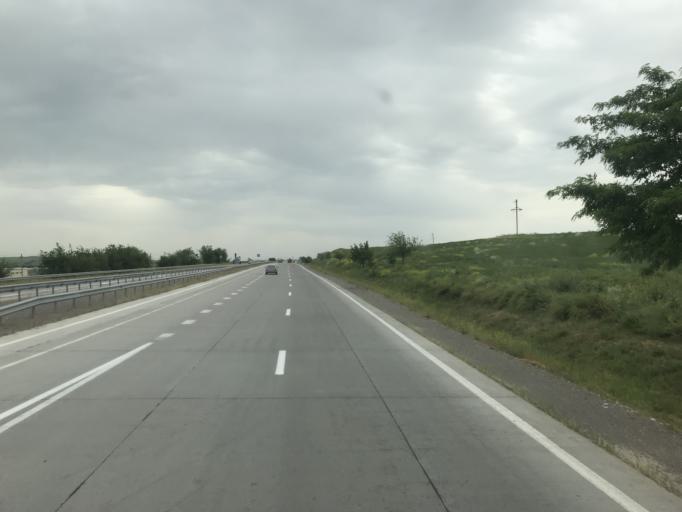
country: KZ
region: Ongtustik Qazaqstan
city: Qazyqurt
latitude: 41.8450
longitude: 69.4062
